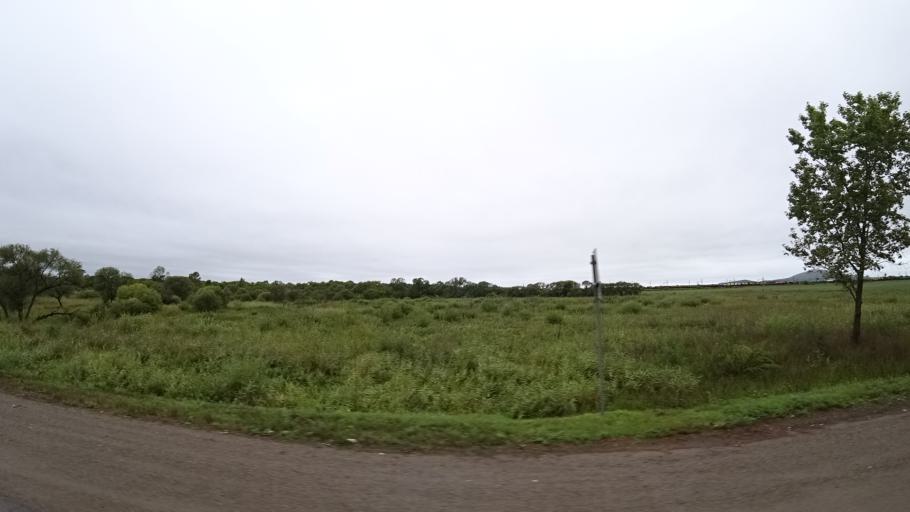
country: RU
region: Primorskiy
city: Monastyrishche
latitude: 44.2212
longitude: 132.4519
